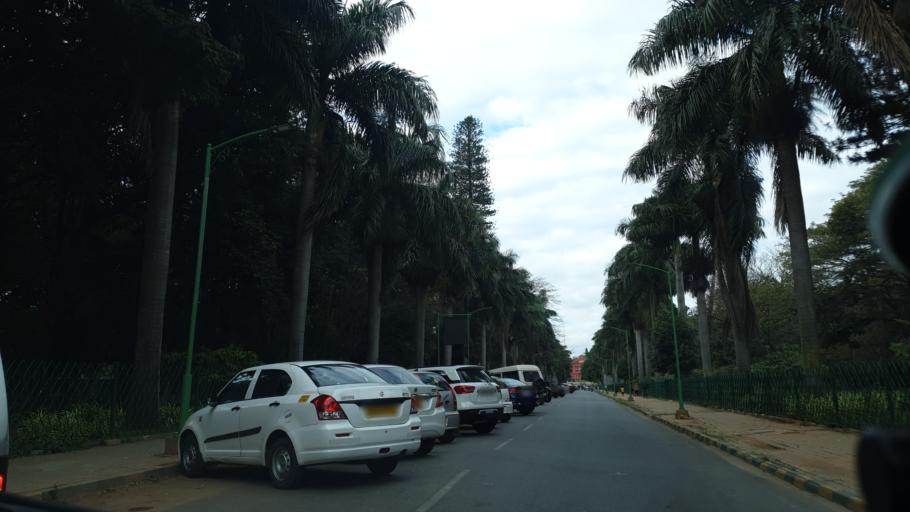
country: IN
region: Karnataka
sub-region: Bangalore Urban
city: Bangalore
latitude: 12.9692
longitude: 77.5892
